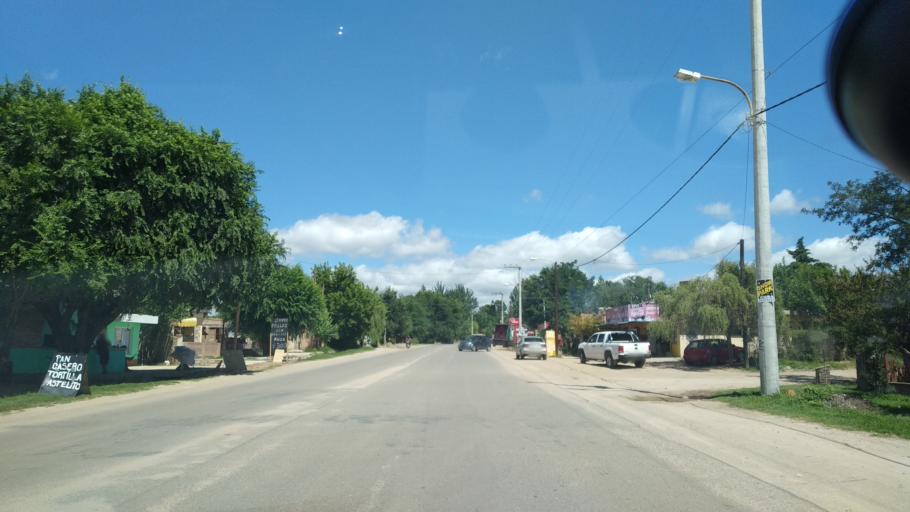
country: AR
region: Cordoba
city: Villa Cura Brochero
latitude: -31.7057
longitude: -65.0222
